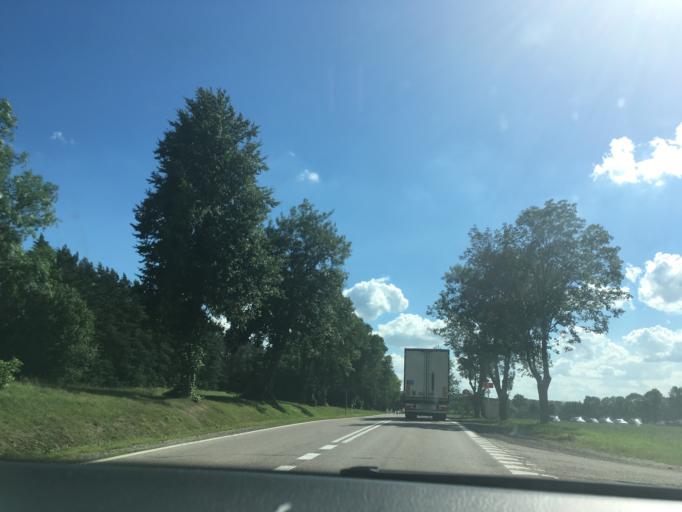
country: PL
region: Podlasie
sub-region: Powiat sokolski
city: Suchowola
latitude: 53.6134
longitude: 23.1205
